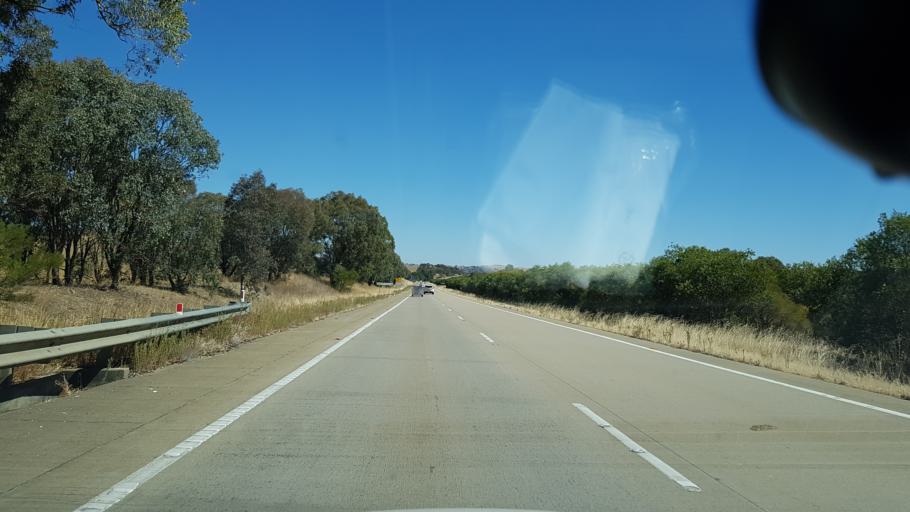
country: AU
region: New South Wales
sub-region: Gundagai
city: Gundagai
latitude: -34.8180
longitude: 148.3857
